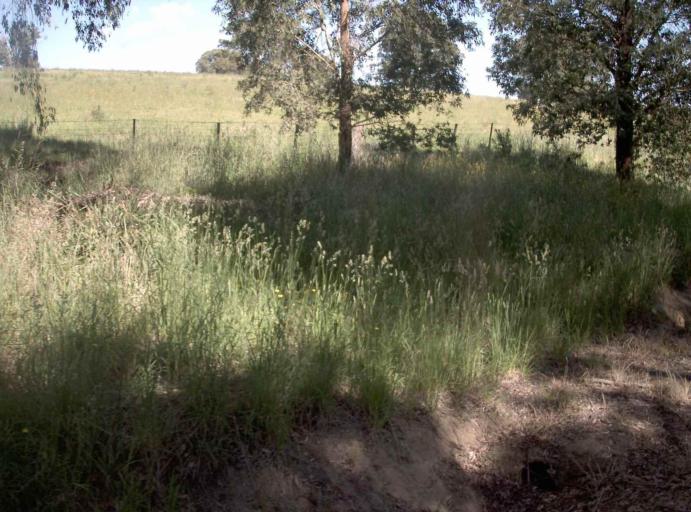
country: AU
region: New South Wales
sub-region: Bombala
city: Bombala
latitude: -37.1761
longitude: 148.7247
